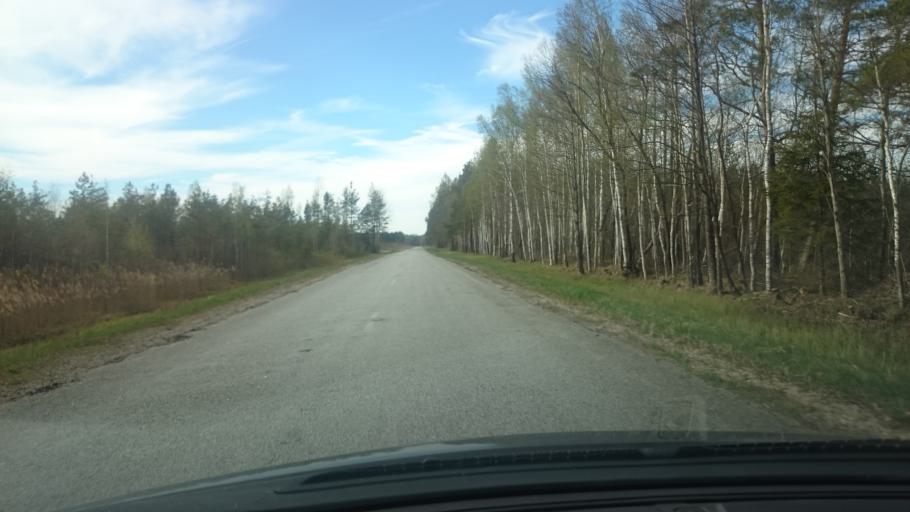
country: EE
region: Ida-Virumaa
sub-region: Toila vald
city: Voka
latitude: 59.1111
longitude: 27.6397
